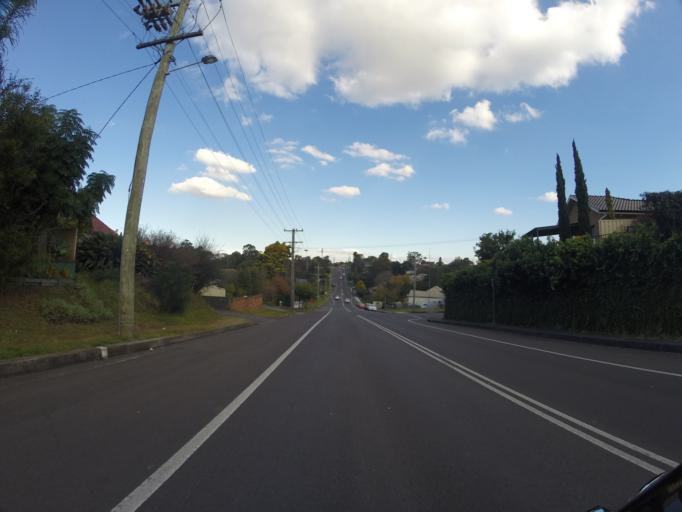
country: AU
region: New South Wales
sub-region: Wollongong
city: Keiraville
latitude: -34.4213
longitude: 150.8690
